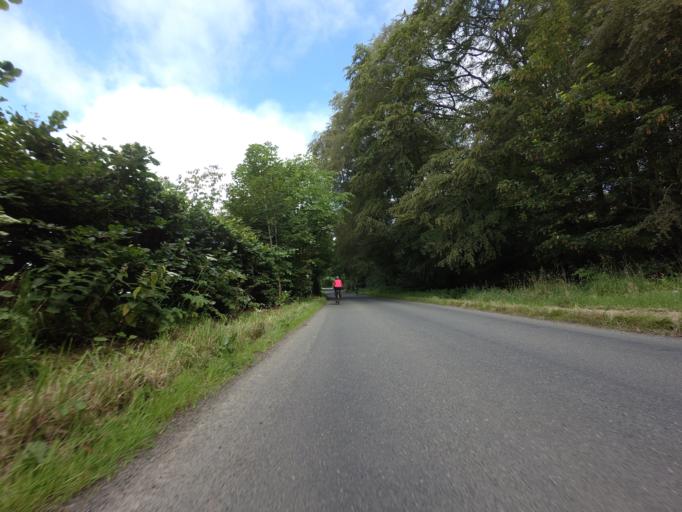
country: GB
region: Scotland
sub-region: Aberdeenshire
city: Turriff
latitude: 57.5507
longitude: -2.4861
